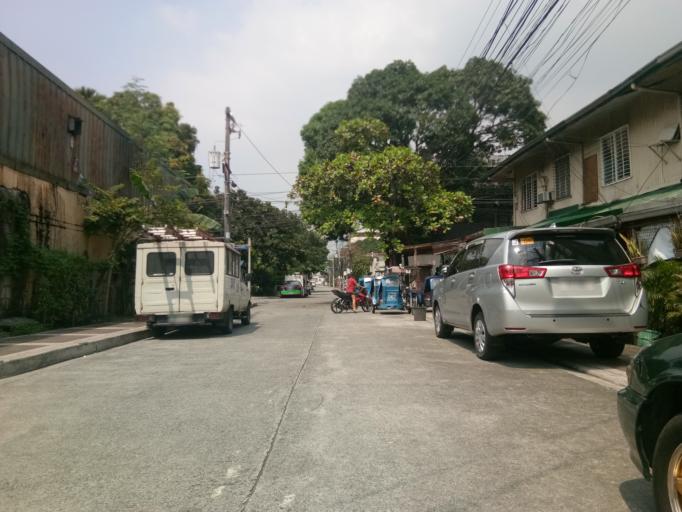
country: PH
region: Metro Manila
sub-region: Marikina
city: Calumpang
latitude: 14.6179
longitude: 121.0613
